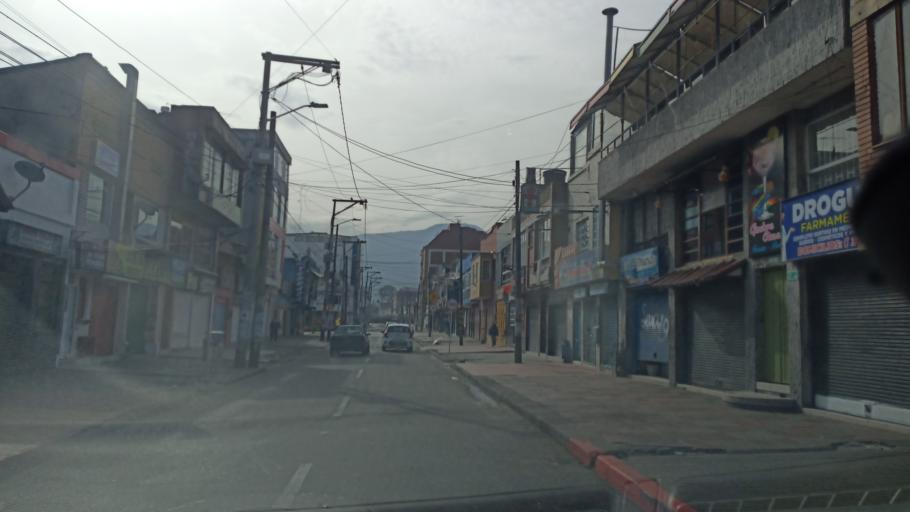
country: CO
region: Bogota D.C.
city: Bogota
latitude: 4.5843
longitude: -74.1009
